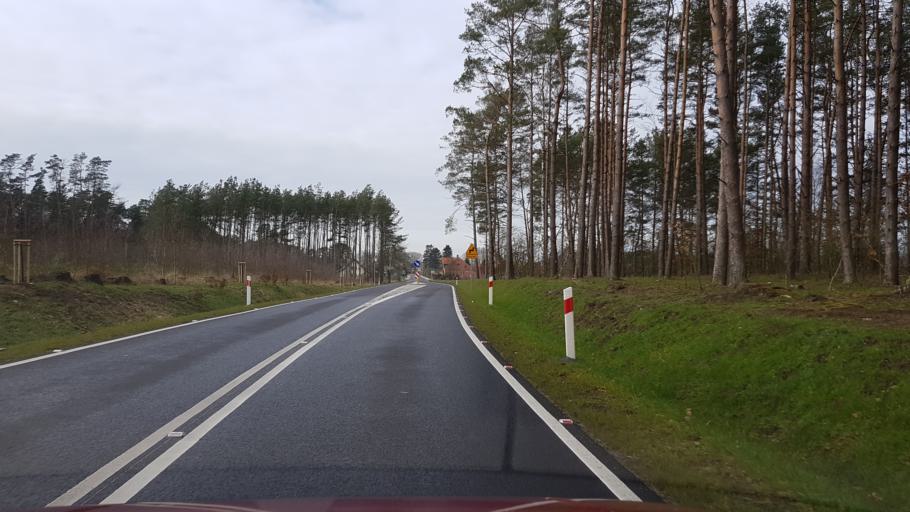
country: PL
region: West Pomeranian Voivodeship
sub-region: Powiat policki
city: Nowe Warpno
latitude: 53.6712
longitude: 14.4003
